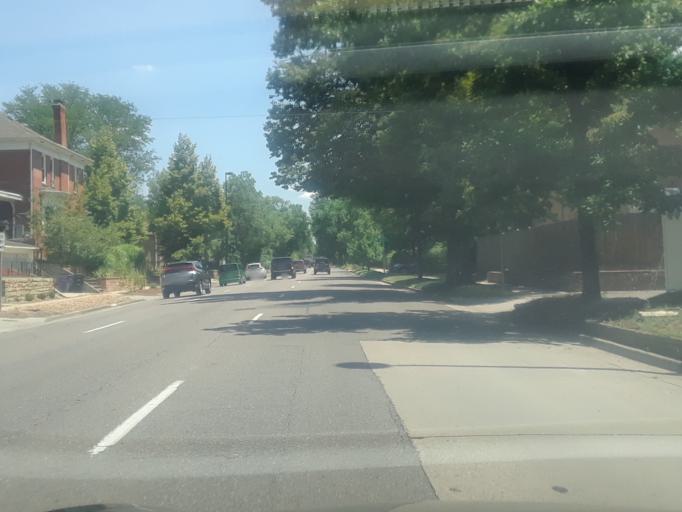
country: US
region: Colorado
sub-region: Denver County
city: Denver
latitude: 39.7255
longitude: -104.9659
